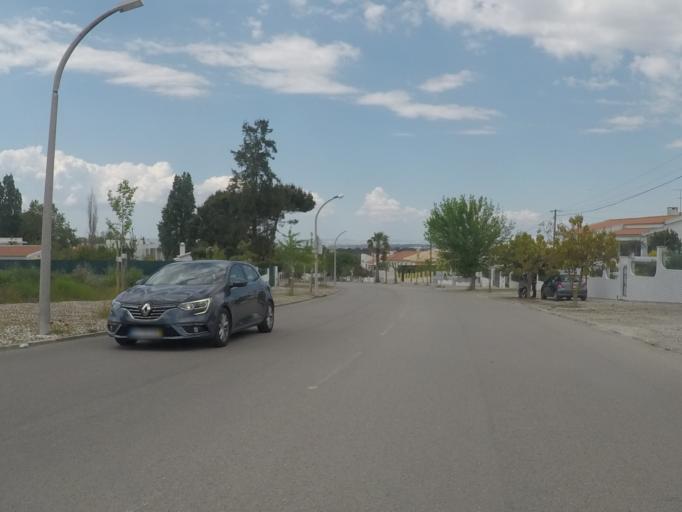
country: PT
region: Setubal
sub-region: Palmela
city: Quinta do Anjo
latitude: 38.5176
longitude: -9.0088
